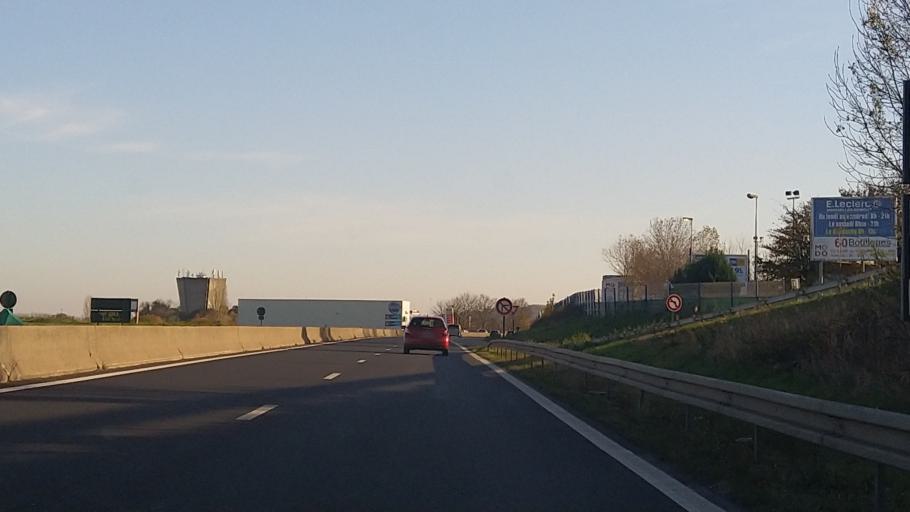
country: FR
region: Ile-de-France
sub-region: Departement du Val-d'Oise
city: Moisselles
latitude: 49.0432
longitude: 2.3391
